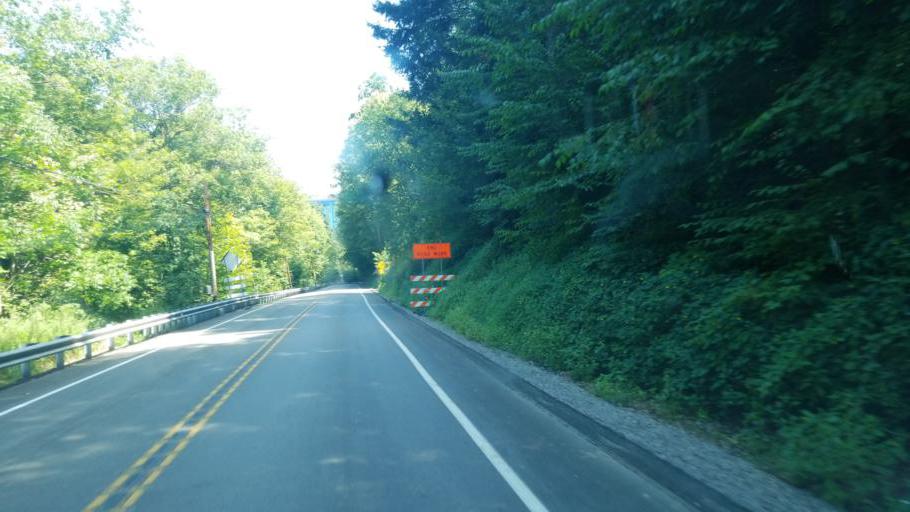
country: US
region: Pennsylvania
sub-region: Clarion County
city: Knox
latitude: 41.1748
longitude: -79.7042
